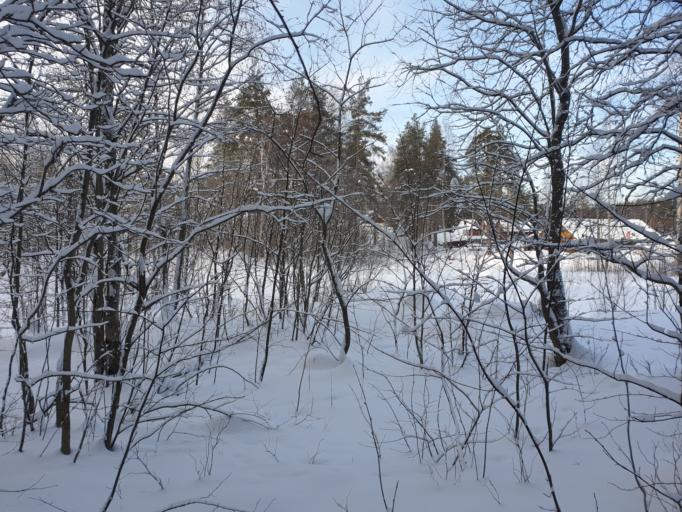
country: RU
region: Republic of Karelia
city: Medvezh'yegorsk
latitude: 62.9168
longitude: 34.4810
